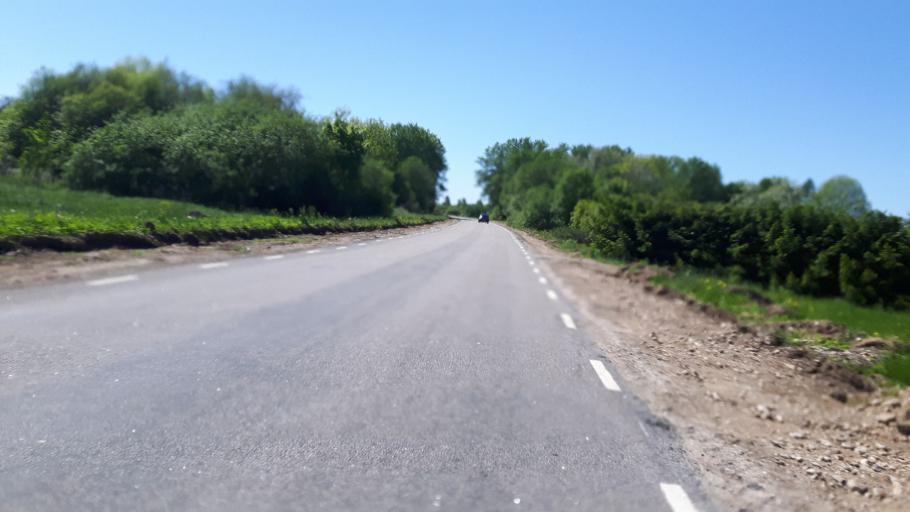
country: EE
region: Ida-Virumaa
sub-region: Narva-Joesuu linn
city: Narva-Joesuu
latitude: 59.3932
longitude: 27.9239
